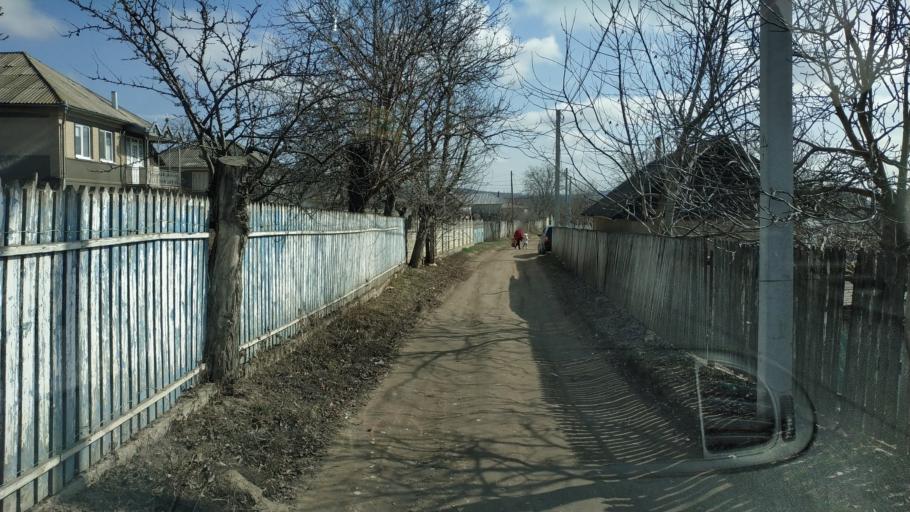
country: MD
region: Hincesti
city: Hincesti
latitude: 46.8289
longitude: 28.6690
